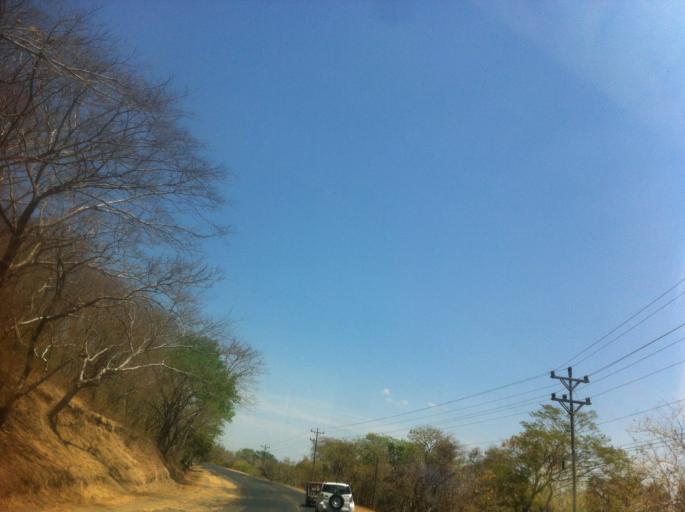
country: CR
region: Guanacaste
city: Belen
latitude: 10.3718
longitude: -85.5775
